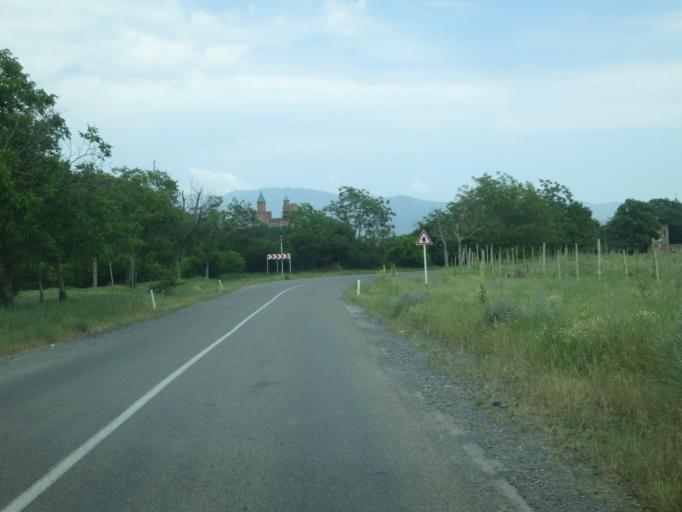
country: GE
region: Kakheti
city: Tsinandali
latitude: 42.0006
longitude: 45.6521
